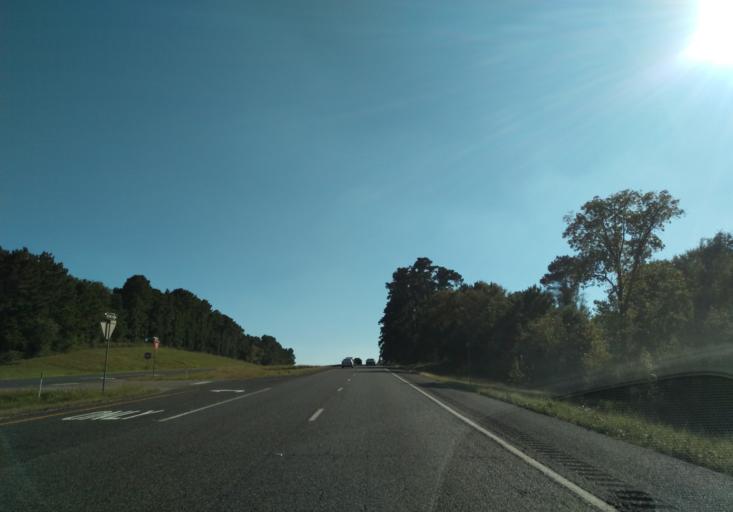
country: US
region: Texas
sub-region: Waller County
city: Hempstead
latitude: 30.2175
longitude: -96.0573
